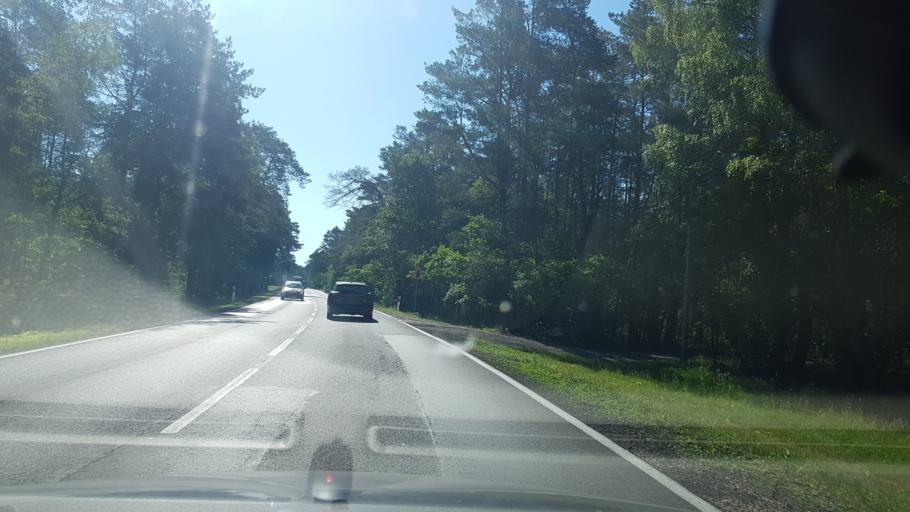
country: PL
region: Masovian Voivodeship
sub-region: Powiat wyszkowski
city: Branszczyk
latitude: 52.5578
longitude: 21.5839
